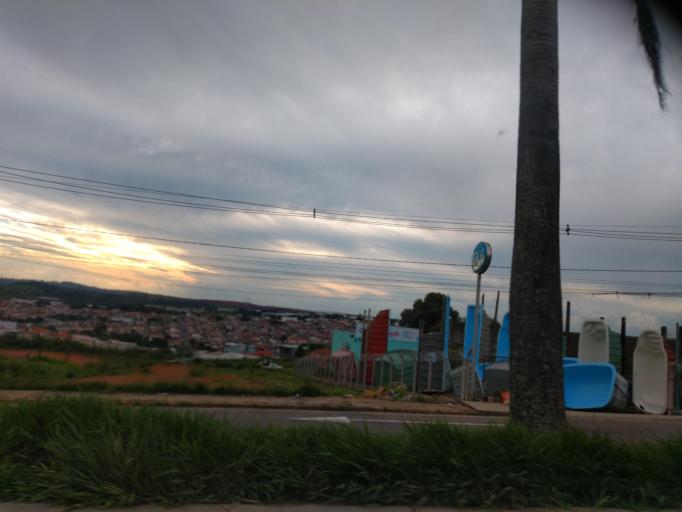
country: BR
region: Minas Gerais
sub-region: Varginha
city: Varginha
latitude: -21.5892
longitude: -45.4374
